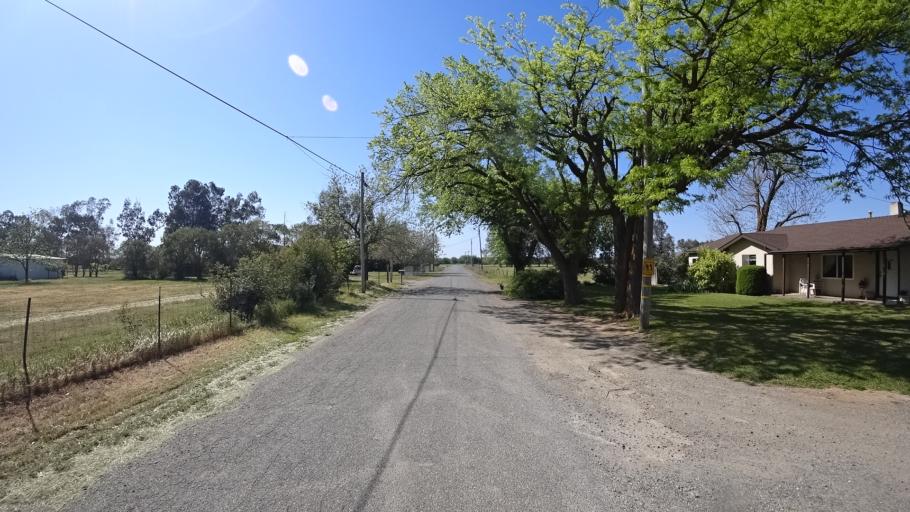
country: US
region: California
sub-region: Glenn County
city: Orland
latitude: 39.7209
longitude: -122.1854
